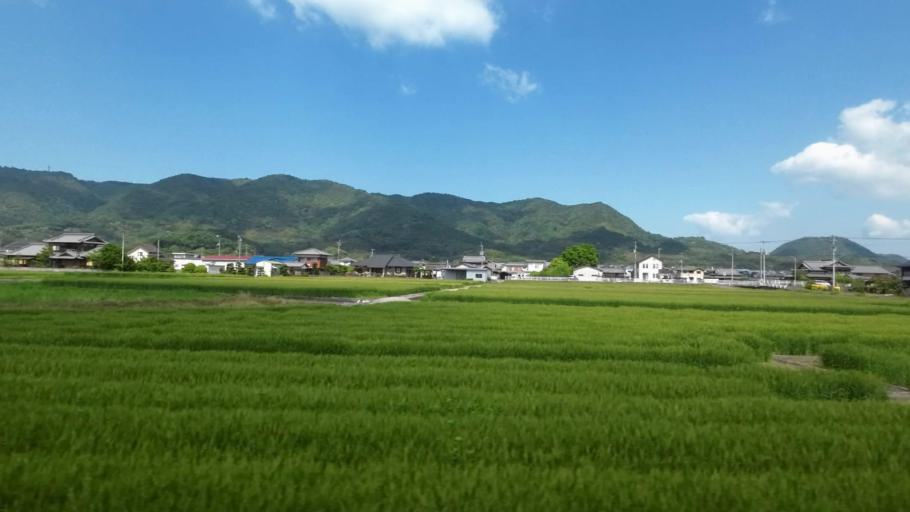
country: JP
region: Kagawa
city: Kan'onjicho
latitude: 34.1732
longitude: 133.6924
